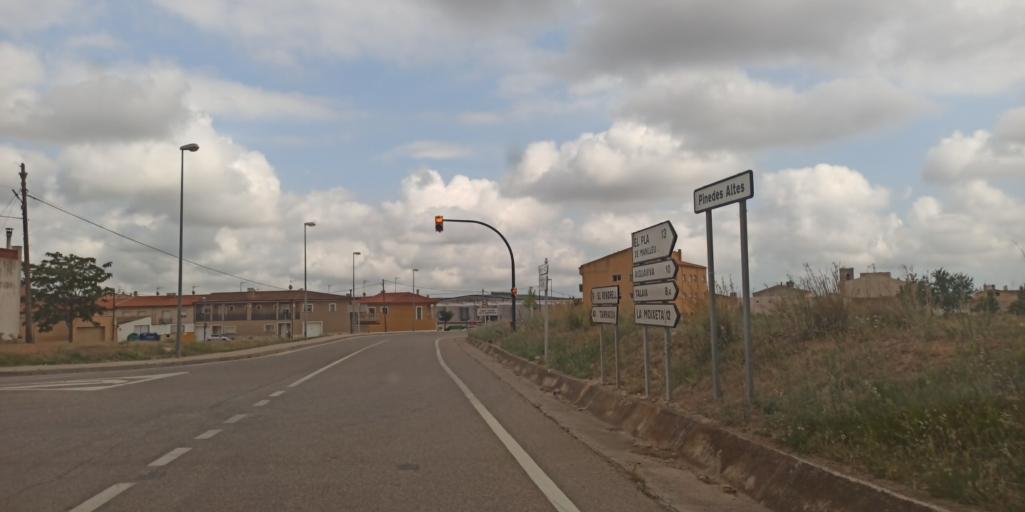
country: ES
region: Catalonia
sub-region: Provincia de Tarragona
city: Sant Jaume dels Domenys
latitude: 41.3027
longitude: 1.5585
